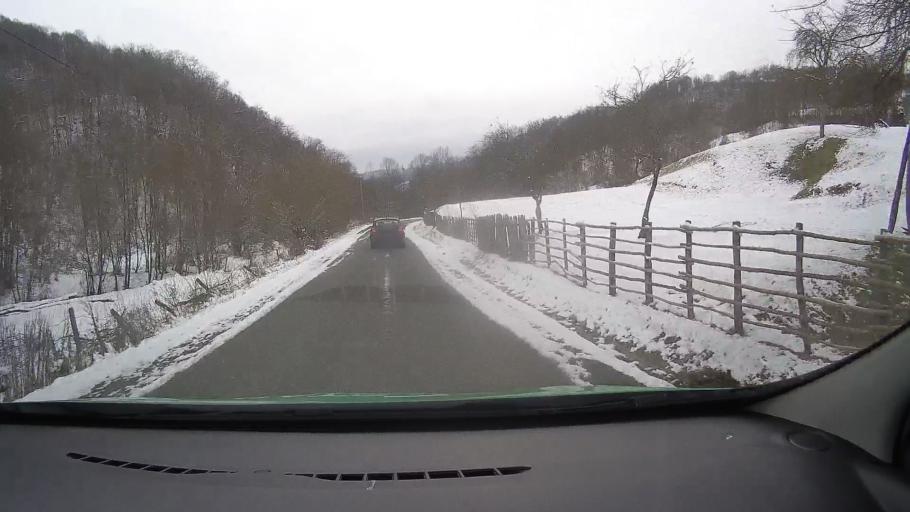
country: RO
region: Alba
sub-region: Comuna Almasu Mare
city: Almasu Mare
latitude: 46.0754
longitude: 23.1087
